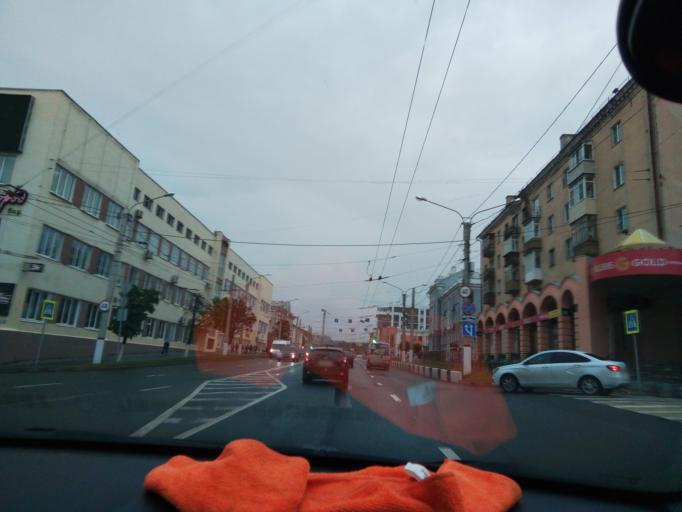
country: RU
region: Chuvashia
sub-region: Cheboksarskiy Rayon
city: Cheboksary
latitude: 56.1439
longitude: 47.2485
